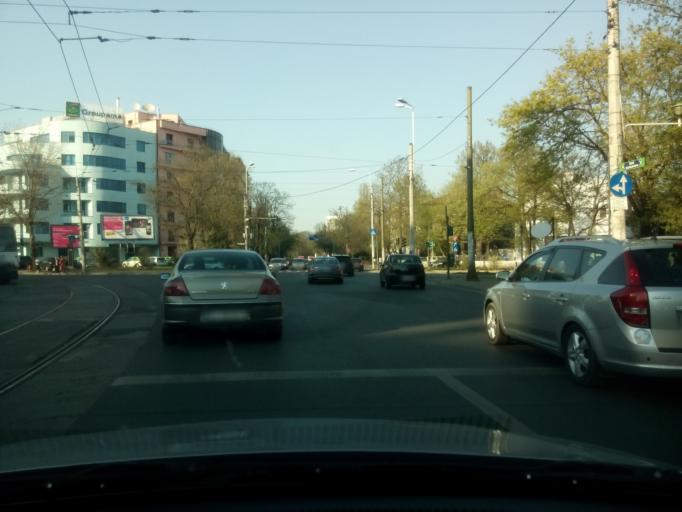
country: RO
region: Bucuresti
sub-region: Municipiul Bucuresti
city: Bucuresti
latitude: 44.4647
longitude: 26.0756
